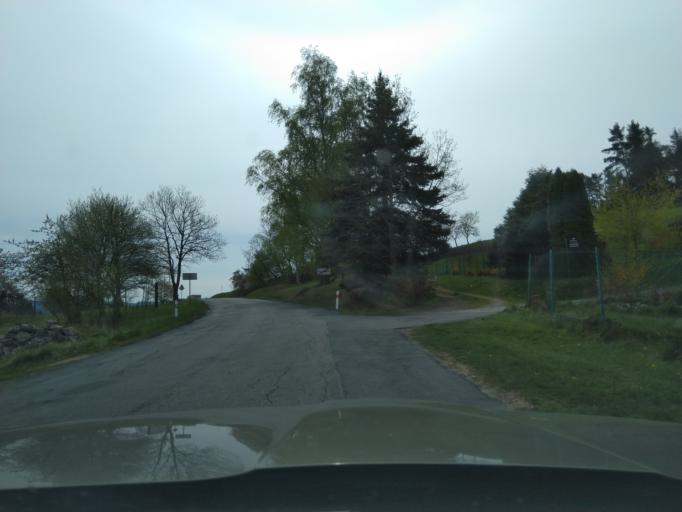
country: CZ
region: Plzensky
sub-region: Okres Klatovy
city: Susice
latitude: 49.2293
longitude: 13.5837
